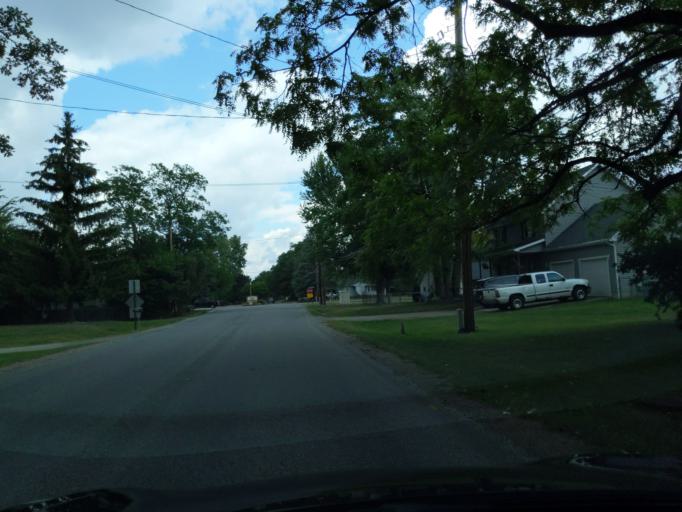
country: US
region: Michigan
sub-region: Ingham County
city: Holt
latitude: 42.6539
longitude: -84.5431
